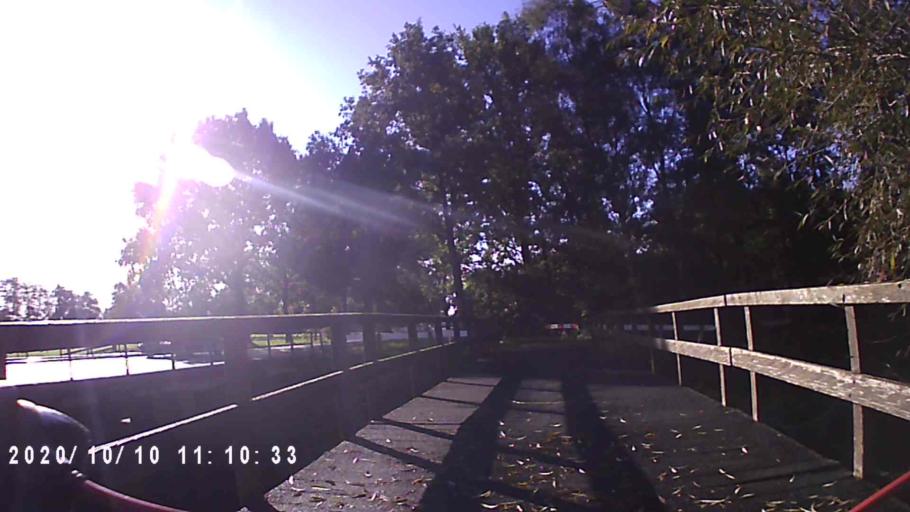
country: NL
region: Friesland
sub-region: Gemeente Smallingerland
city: Drachtstercompagnie
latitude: 53.1155
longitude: 6.2061
